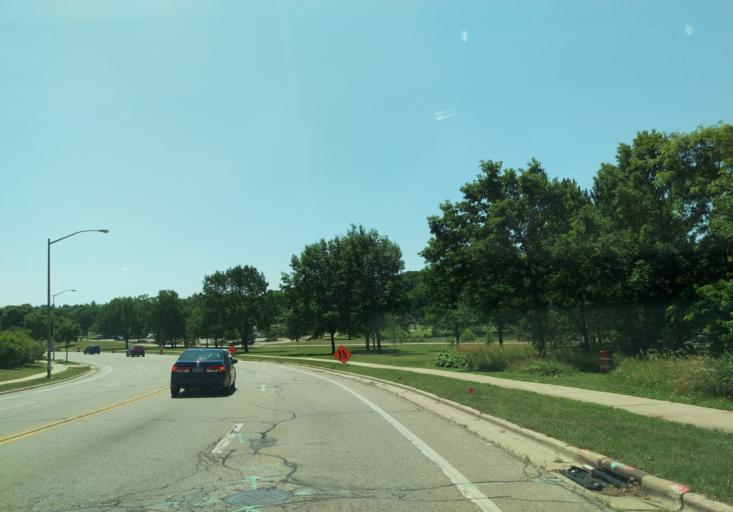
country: US
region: Wisconsin
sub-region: Dane County
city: Verona
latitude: 43.0401
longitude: -89.5048
